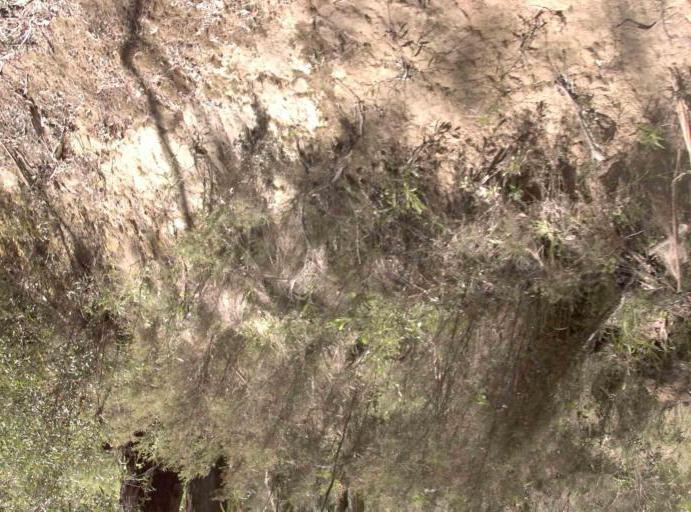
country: AU
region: Victoria
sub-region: East Gippsland
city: Lakes Entrance
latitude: -37.2260
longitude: 148.2636
